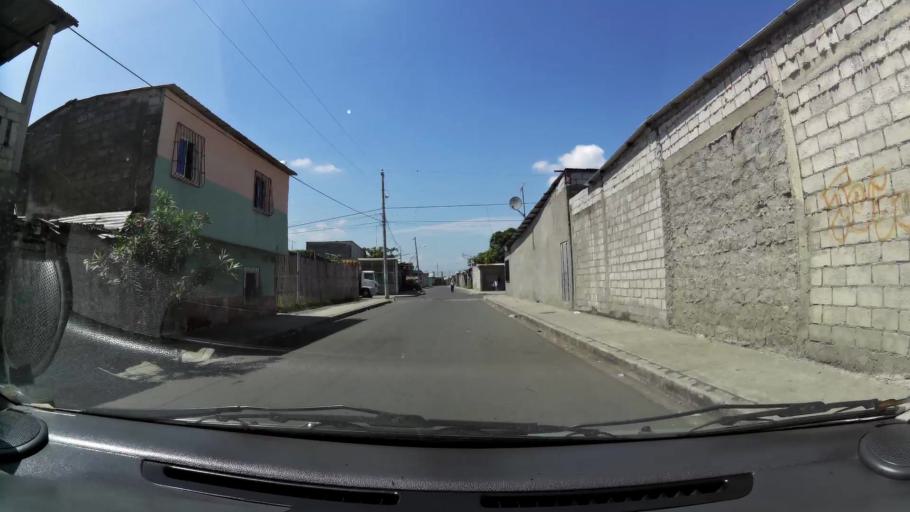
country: EC
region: Guayas
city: Guayaquil
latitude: -2.2304
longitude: -79.9199
